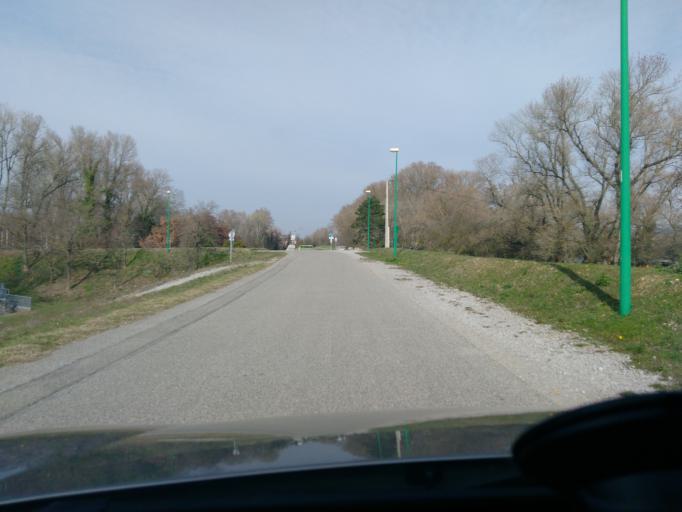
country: FR
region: Rhone-Alpes
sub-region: Departement de l'Ardeche
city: Cruas
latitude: 44.6547
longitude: 4.7764
